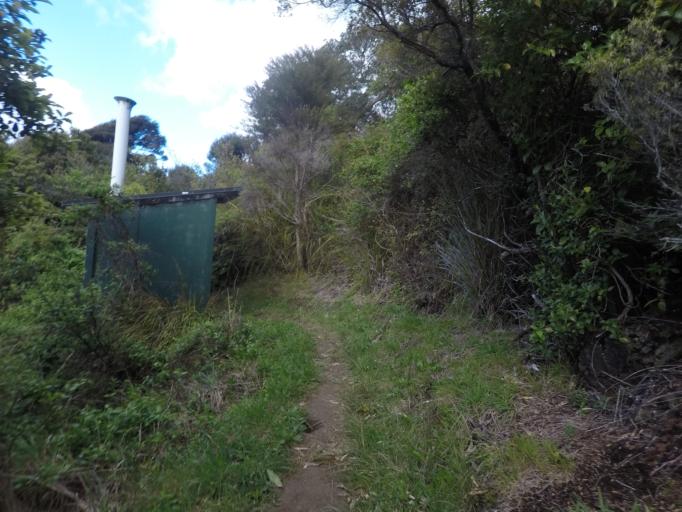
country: NZ
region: Bay of Plenty
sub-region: Western Bay of Plenty District
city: Waihi Beach
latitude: -37.3873
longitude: 175.9400
